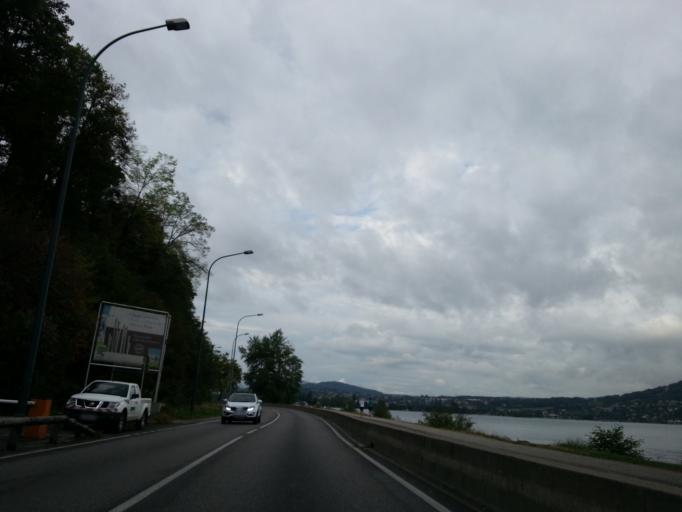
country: FR
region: Rhone-Alpes
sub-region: Departement de la Haute-Savoie
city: Sevrier
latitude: 45.8887
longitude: 6.1436
